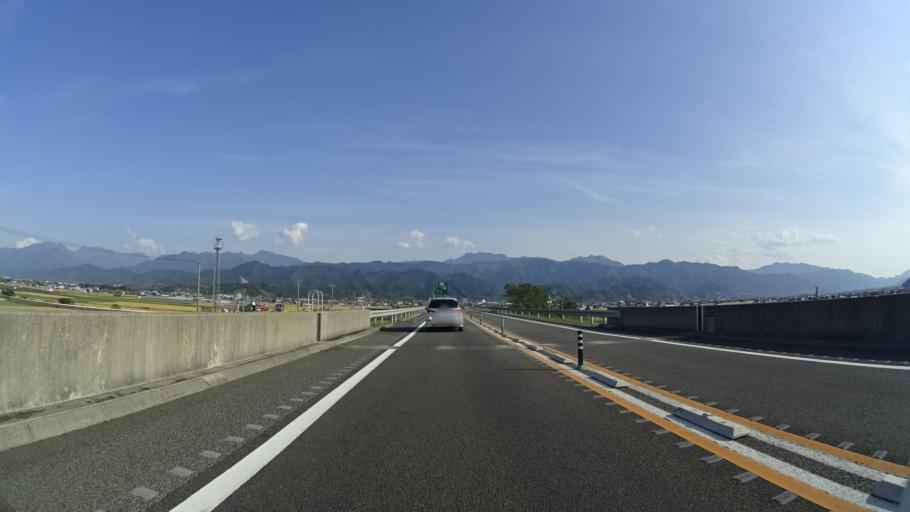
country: JP
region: Ehime
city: Saijo
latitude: 33.9089
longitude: 133.0736
